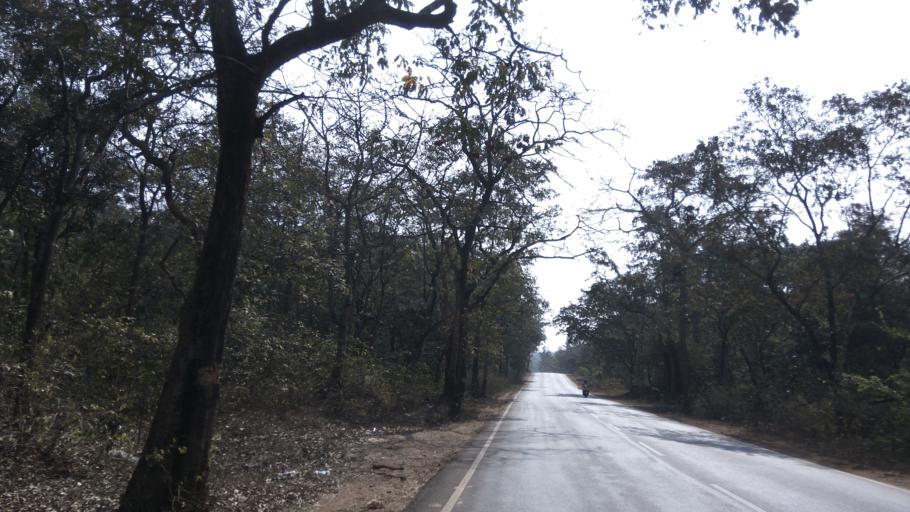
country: IN
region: Goa
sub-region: North Goa
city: Palle
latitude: 15.3813
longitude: 74.1432
